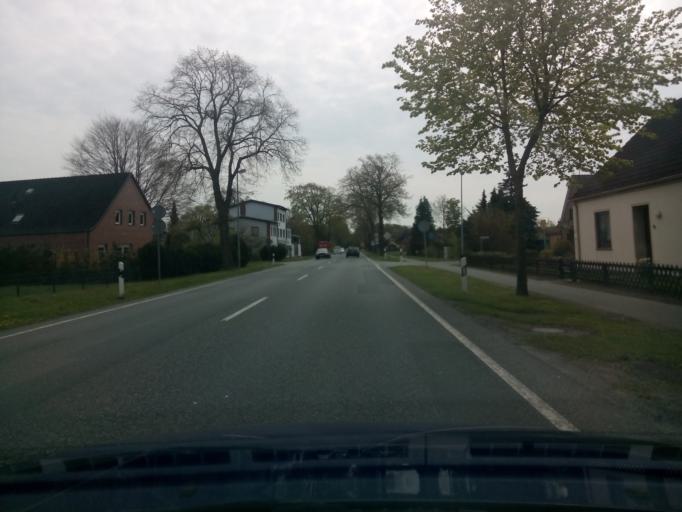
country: DE
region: Lower Saxony
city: Syke
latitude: 52.9675
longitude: 8.7963
